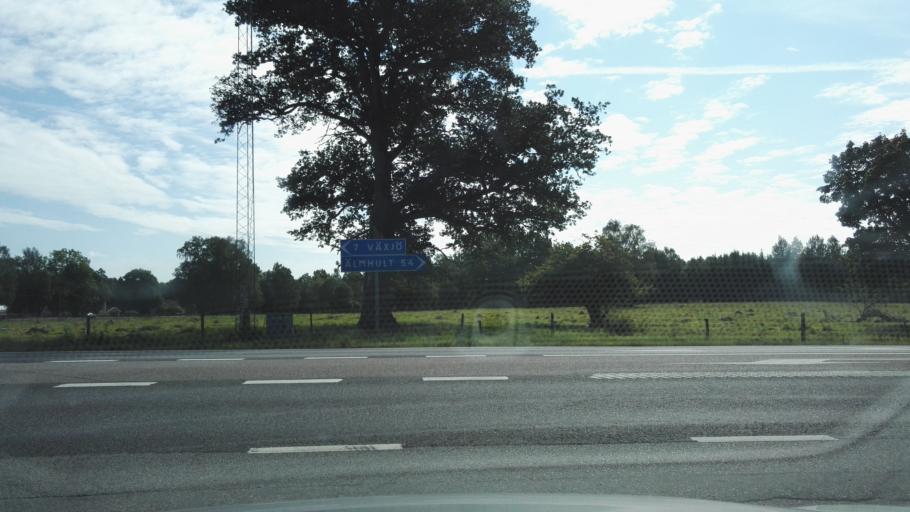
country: SE
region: Kronoberg
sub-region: Vaxjo Kommun
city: Vaexjoe
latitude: 56.8667
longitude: 14.7367
